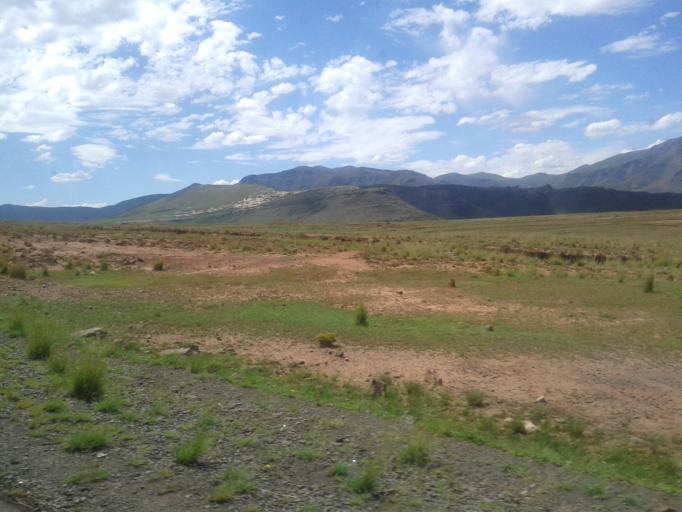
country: LS
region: Qacha's Nek
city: Qacha's Nek
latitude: -30.0364
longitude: 28.3335
